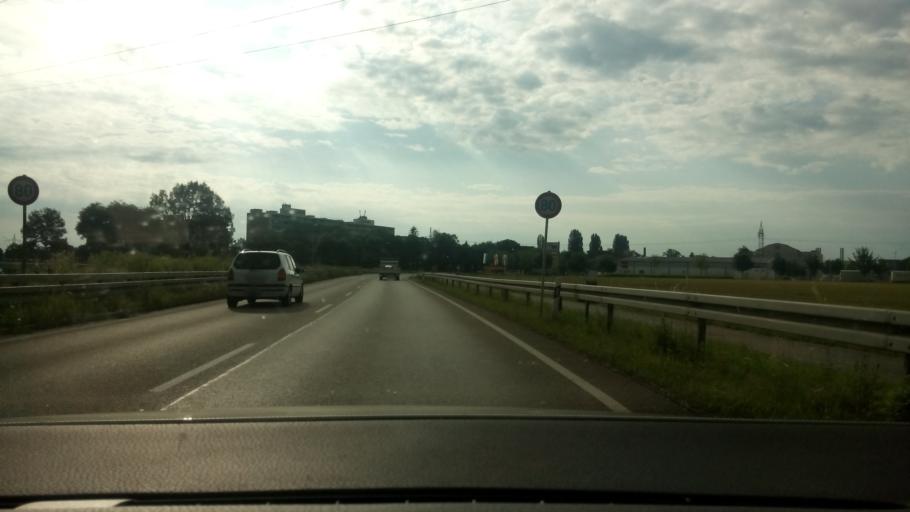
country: DE
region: Bavaria
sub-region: Upper Bavaria
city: Karlsfeld
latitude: 48.2287
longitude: 11.4595
